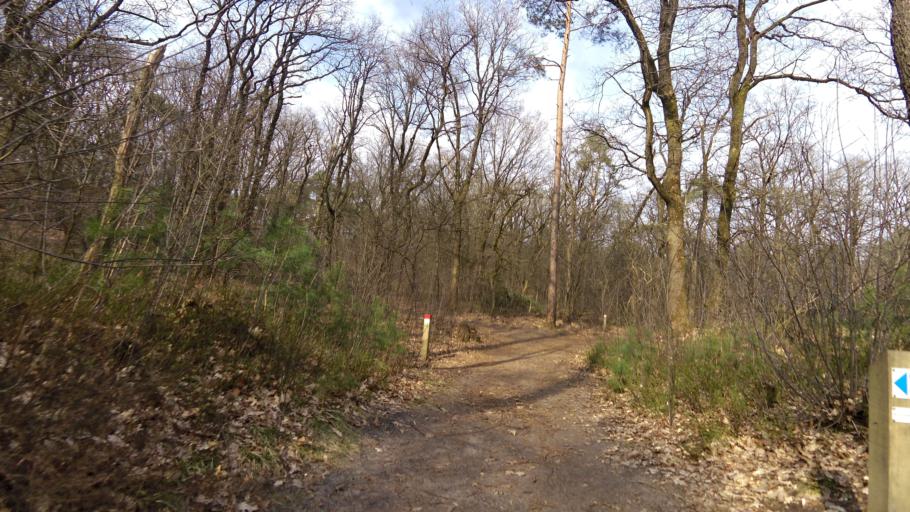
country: NL
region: Gelderland
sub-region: Gemeente Ede
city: Otterlo
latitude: 52.0896
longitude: 5.7865
